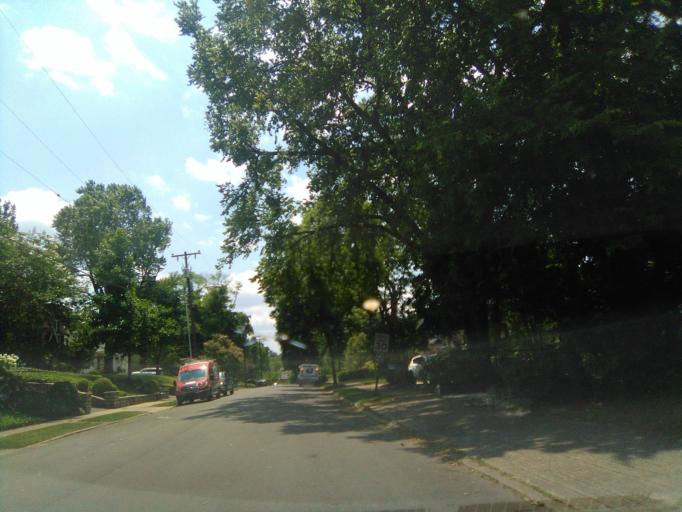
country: US
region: Tennessee
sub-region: Davidson County
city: Belle Meade
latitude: 36.1313
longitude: -86.8288
